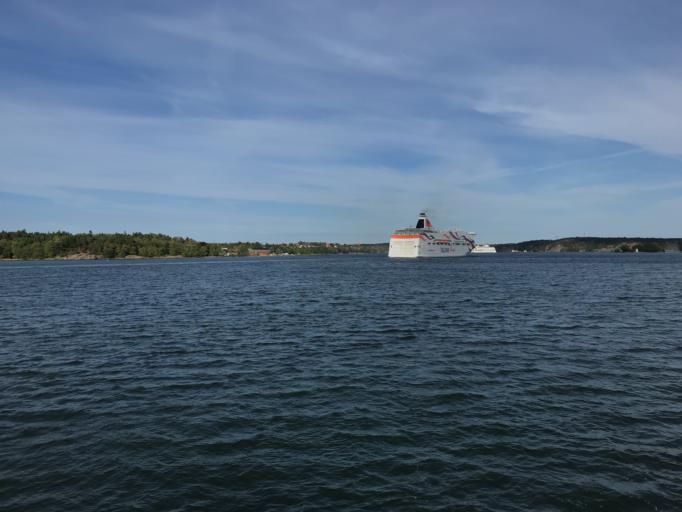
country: SE
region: Stockholm
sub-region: Nacka Kommun
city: Nacka
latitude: 59.3360
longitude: 18.1539
